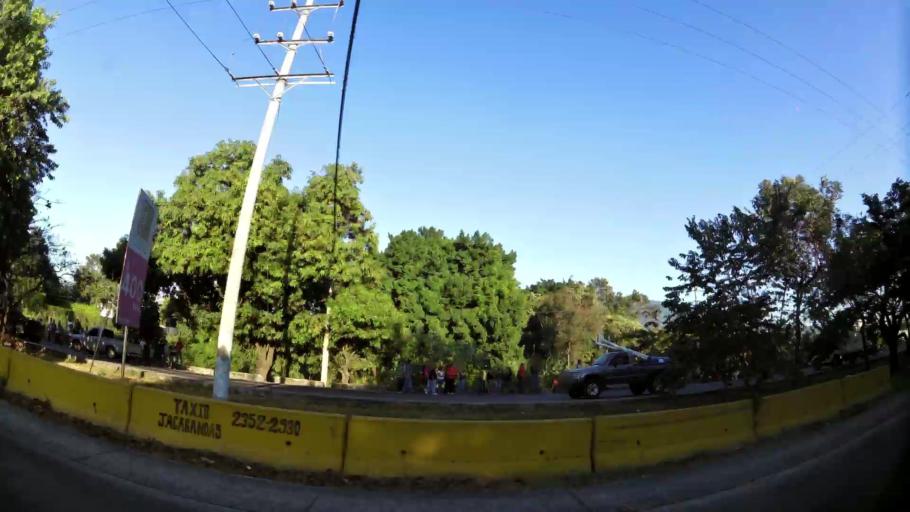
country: SV
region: La Libertad
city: Santa Tecla
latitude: 13.7496
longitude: -89.3651
